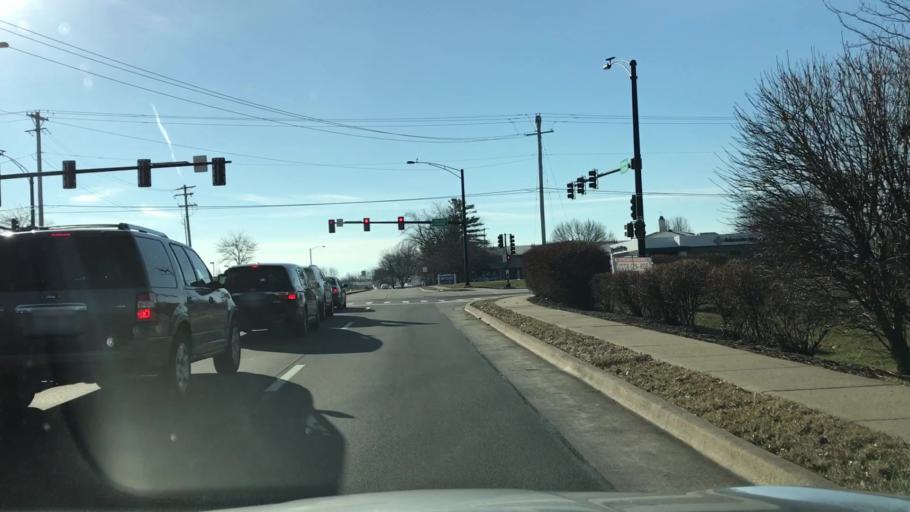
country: US
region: Illinois
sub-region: McLean County
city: Normal
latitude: 40.5109
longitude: -88.9608
